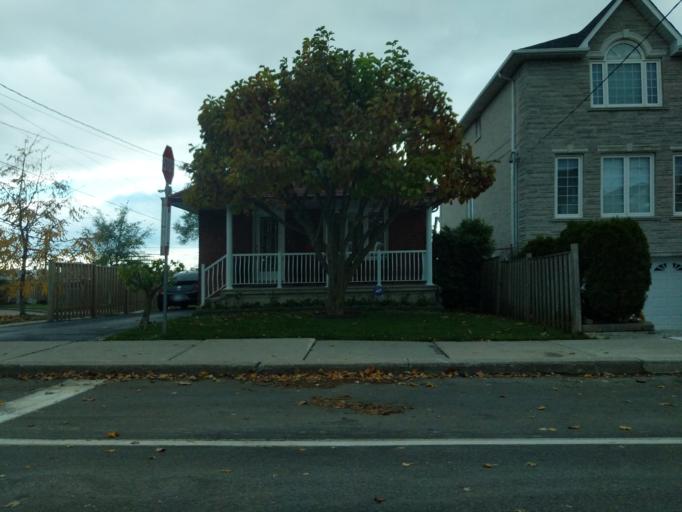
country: CA
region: Ontario
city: Toronto
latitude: 43.7055
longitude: -79.4611
